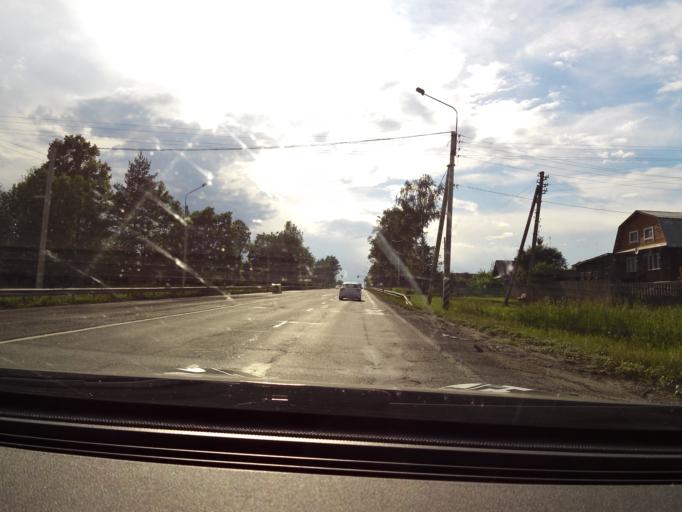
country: RU
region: Vladimir
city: Gorokhovets
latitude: 56.1687
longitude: 42.4495
